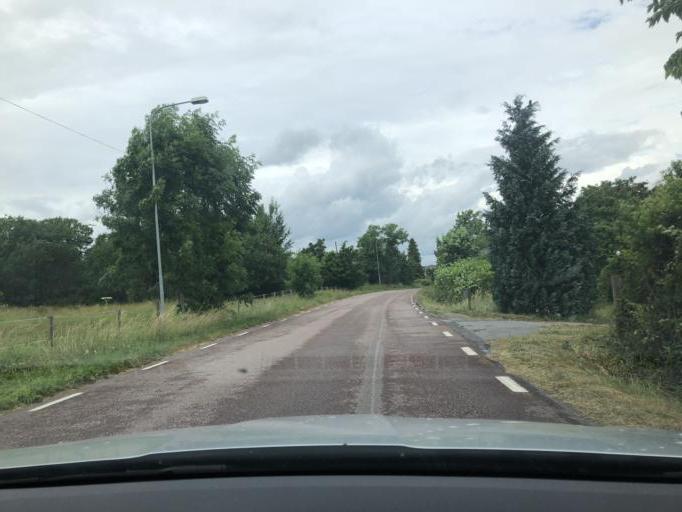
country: SE
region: Blekinge
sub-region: Solvesborgs Kommun
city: Soelvesborg
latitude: 56.1493
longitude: 14.6030
